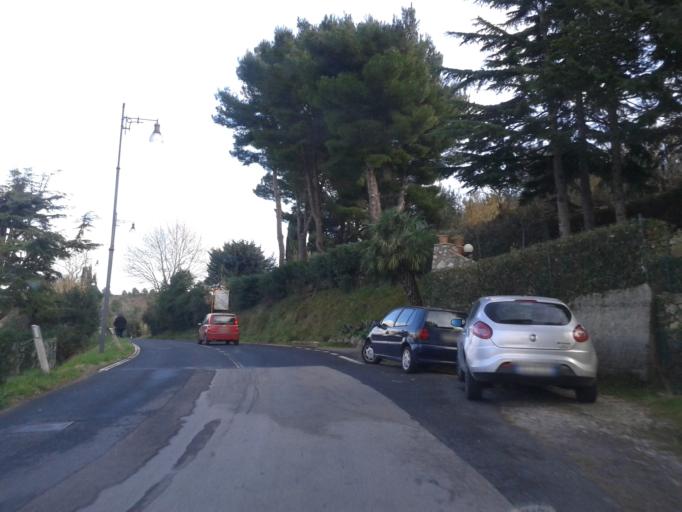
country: IT
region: Tuscany
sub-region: Provincia di Livorno
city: Quercianella
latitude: 43.4997
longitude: 10.3540
